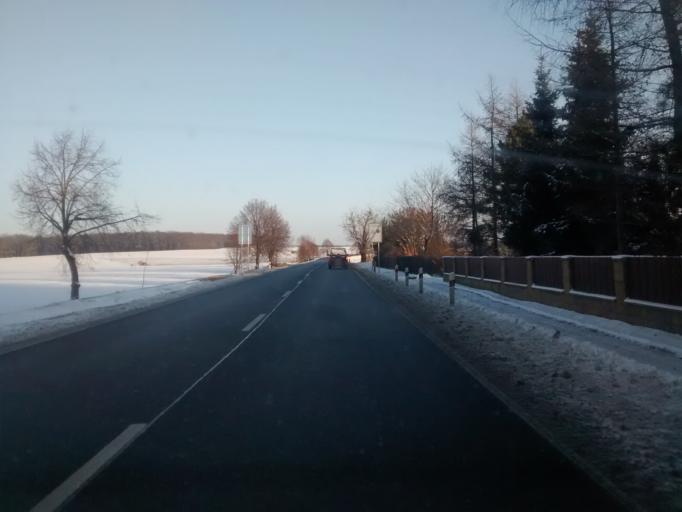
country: CZ
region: Central Bohemia
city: Tisice
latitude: 50.3228
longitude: 14.5578
